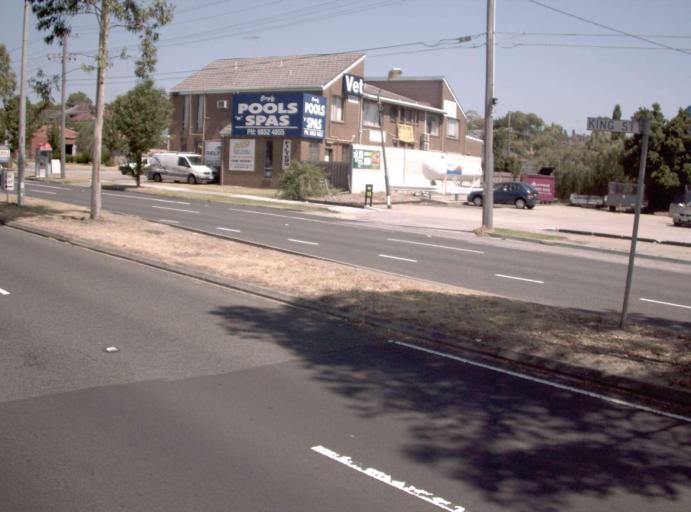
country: AU
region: Victoria
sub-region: Manningham
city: Bulleen
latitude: -37.7627
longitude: 145.0839
